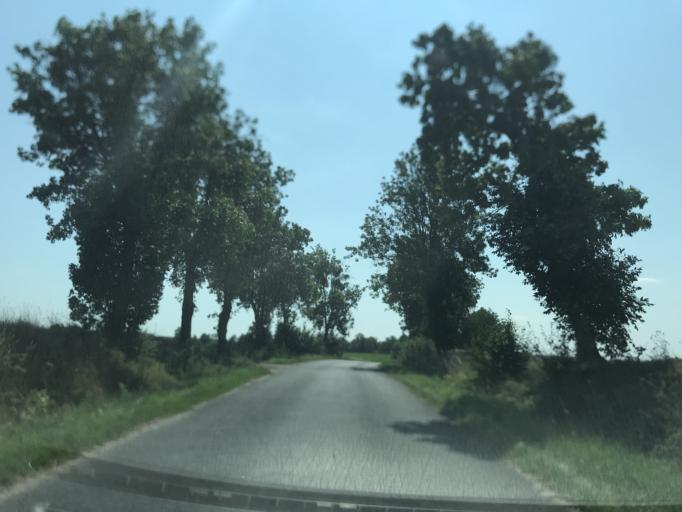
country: PL
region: Kujawsko-Pomorskie
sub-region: Powiat lipnowski
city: Chrostkowo
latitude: 52.9689
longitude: 19.2057
